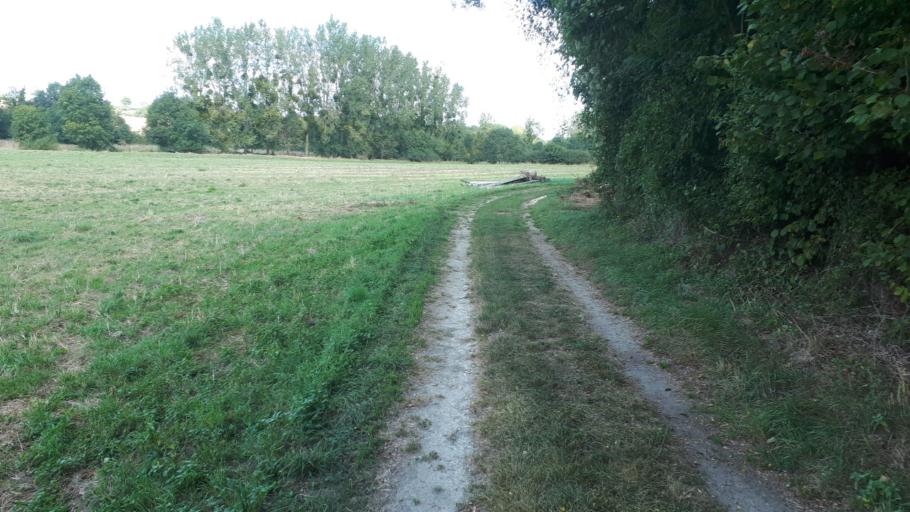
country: FR
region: Centre
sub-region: Departement du Loir-et-Cher
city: Villiers-sur-Loir
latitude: 47.8163
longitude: 0.9617
